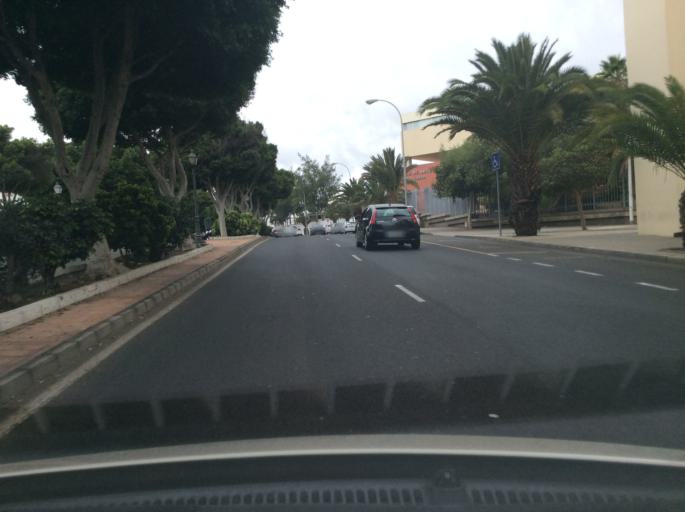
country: ES
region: Canary Islands
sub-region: Provincia de Las Palmas
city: Arrecife
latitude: 28.9660
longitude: -13.5551
